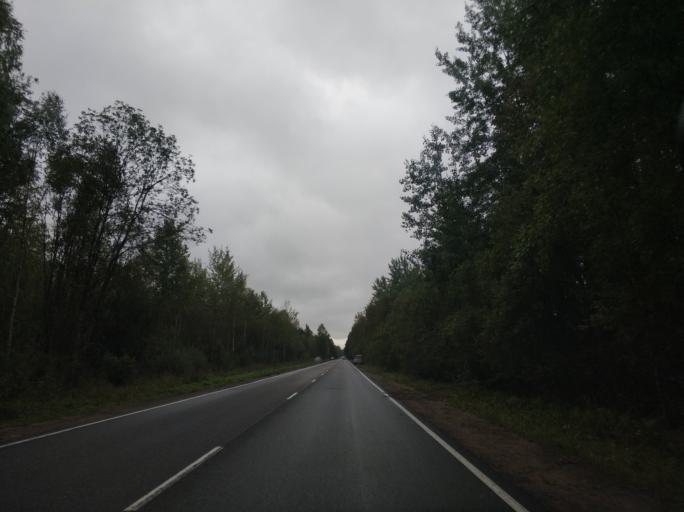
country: RU
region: Leningrad
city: Borisova Griva
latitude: 60.1450
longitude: 30.9453
